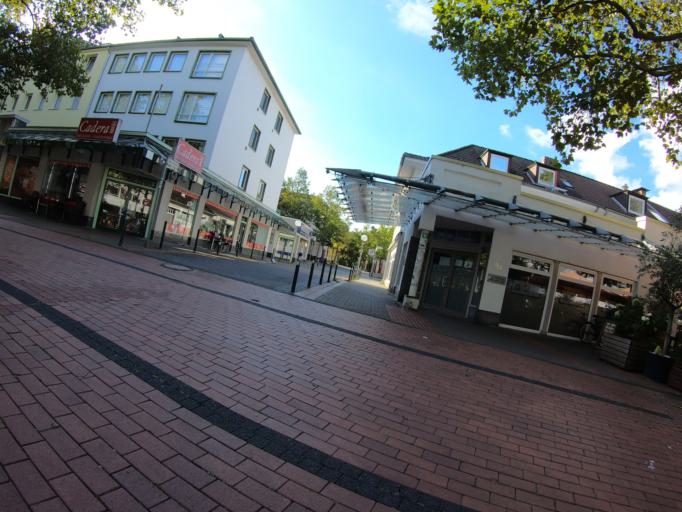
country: DE
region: Lower Saxony
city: Wolfsburg
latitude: 52.4196
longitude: 10.7850
